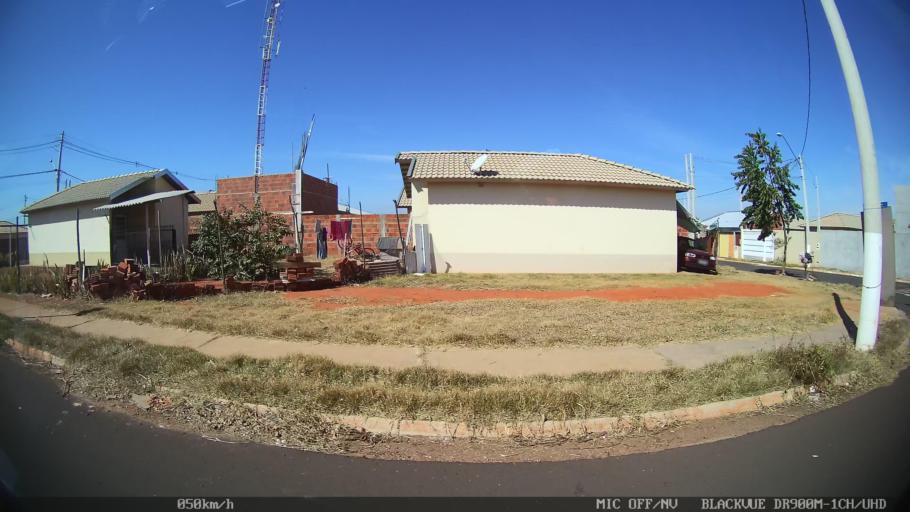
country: BR
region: Sao Paulo
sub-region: Sao Jose Do Rio Preto
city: Sao Jose do Rio Preto
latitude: -20.7503
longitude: -49.4400
